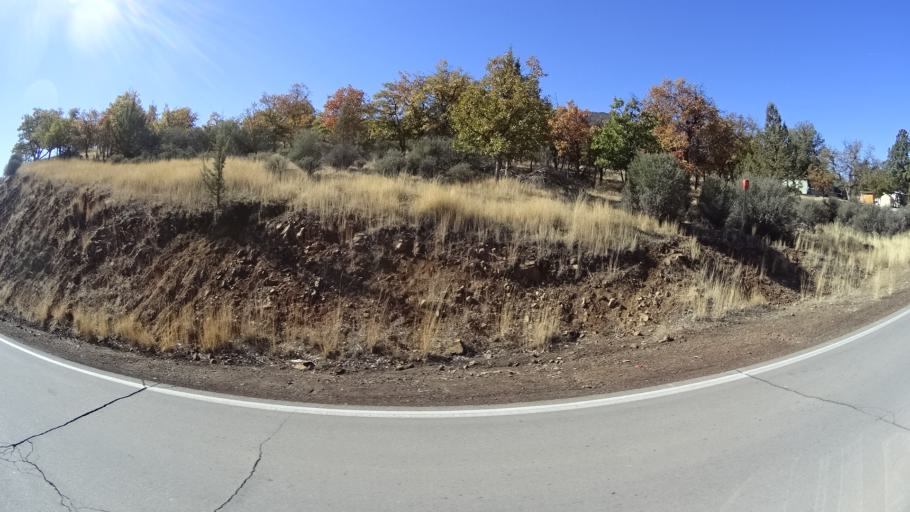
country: US
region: California
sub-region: Siskiyou County
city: Montague
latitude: 41.8807
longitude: -122.4811
